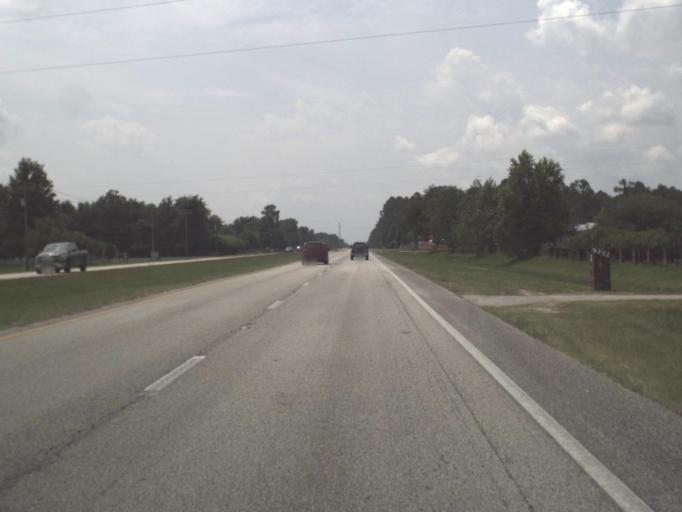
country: US
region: Florida
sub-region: Clay County
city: Green Cove Springs
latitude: 29.9100
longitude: -81.6781
